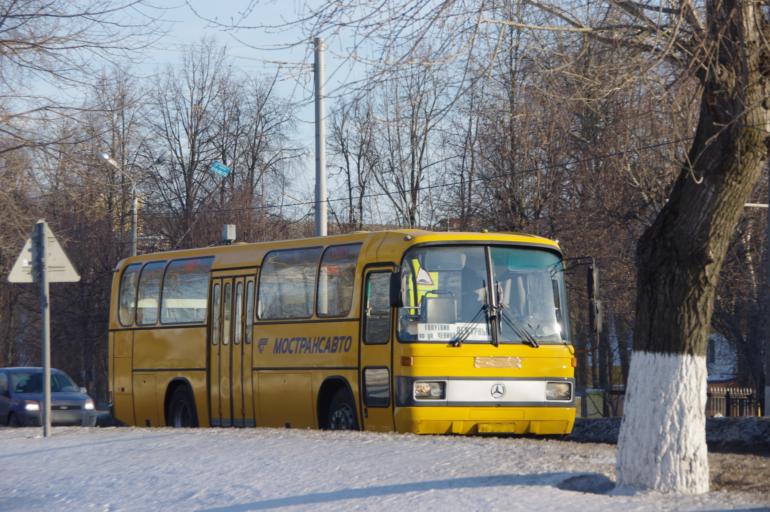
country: RU
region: Moskovskaya
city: Kolomna
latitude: 55.0904
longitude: 38.7823
